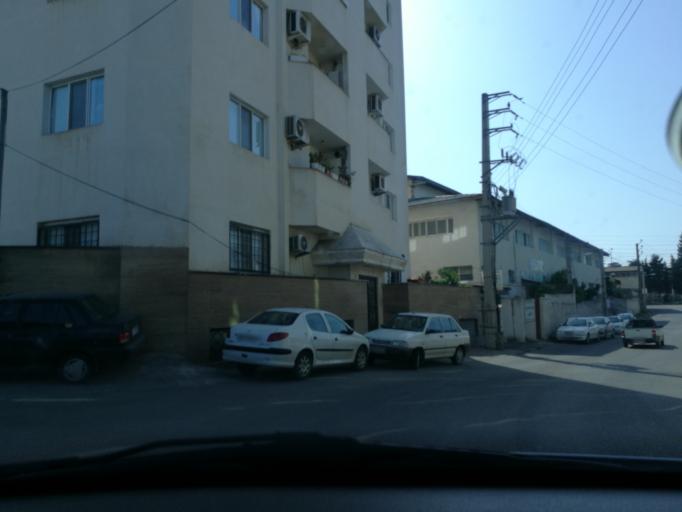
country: IR
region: Mazandaran
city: Chalus
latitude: 36.6597
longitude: 51.4250
